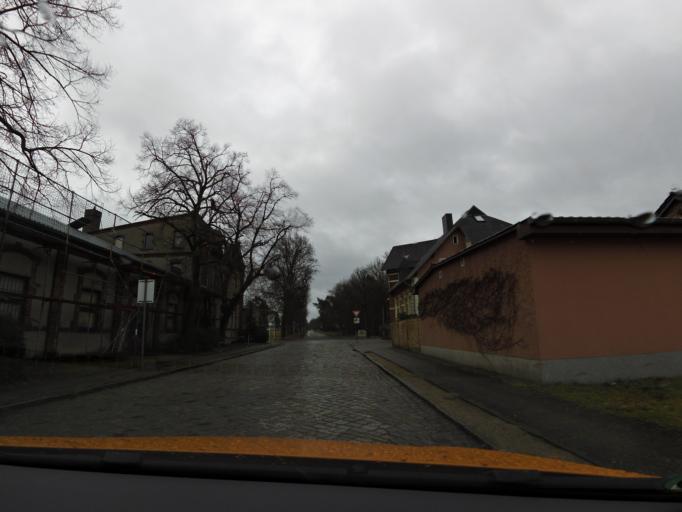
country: DE
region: Brandenburg
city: Sperenberg
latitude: 52.1654
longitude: 13.3666
